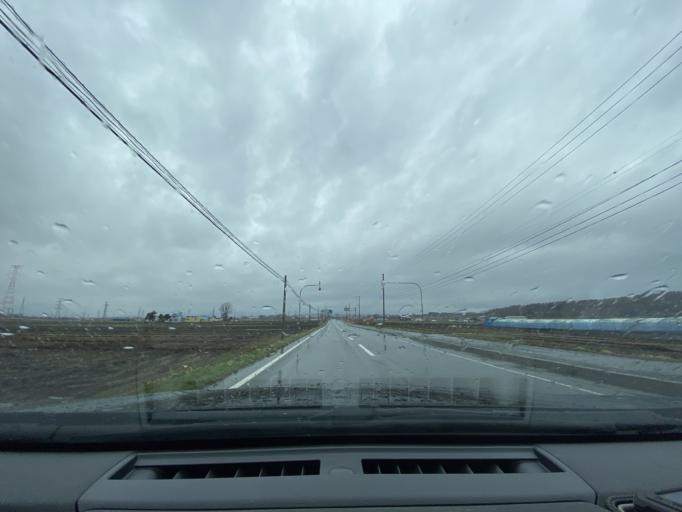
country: JP
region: Hokkaido
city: Fukagawa
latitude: 43.8140
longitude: 141.9678
